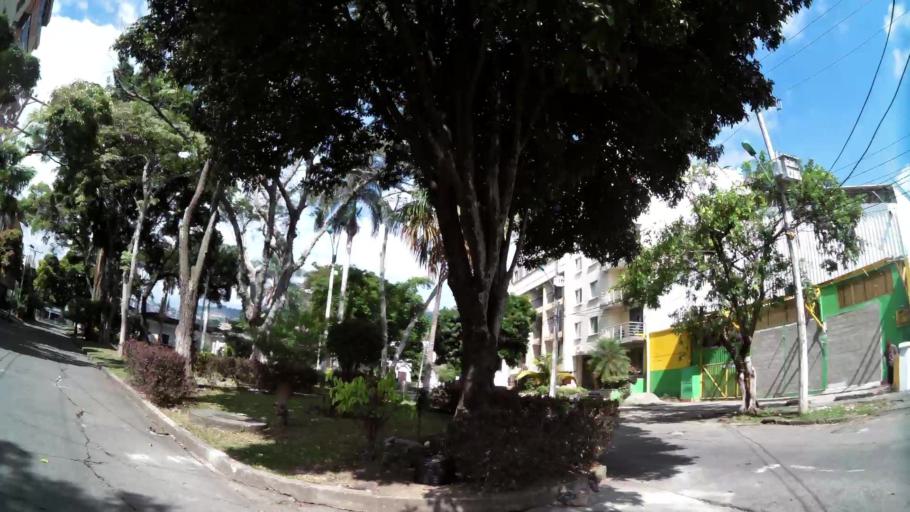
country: CO
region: Valle del Cauca
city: Cali
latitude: 3.4318
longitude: -76.5396
